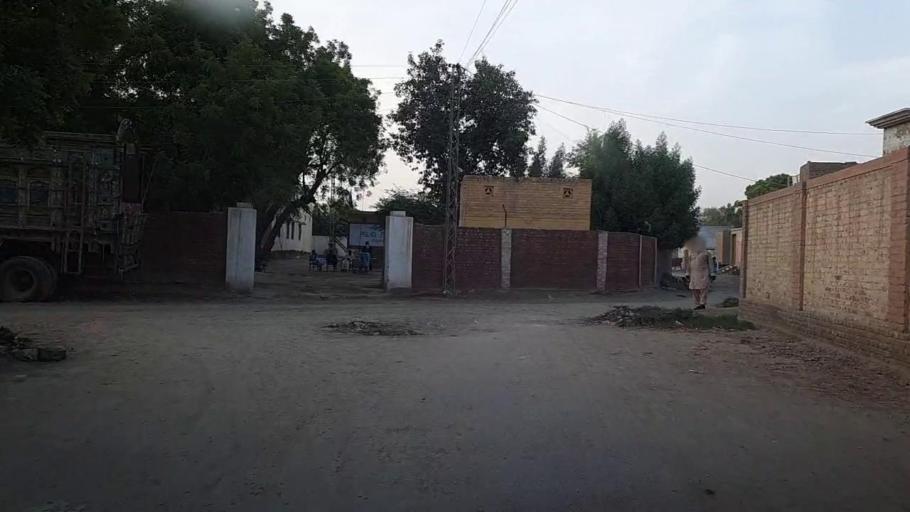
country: PK
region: Sindh
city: Ubauro
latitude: 28.2971
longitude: 69.7991
